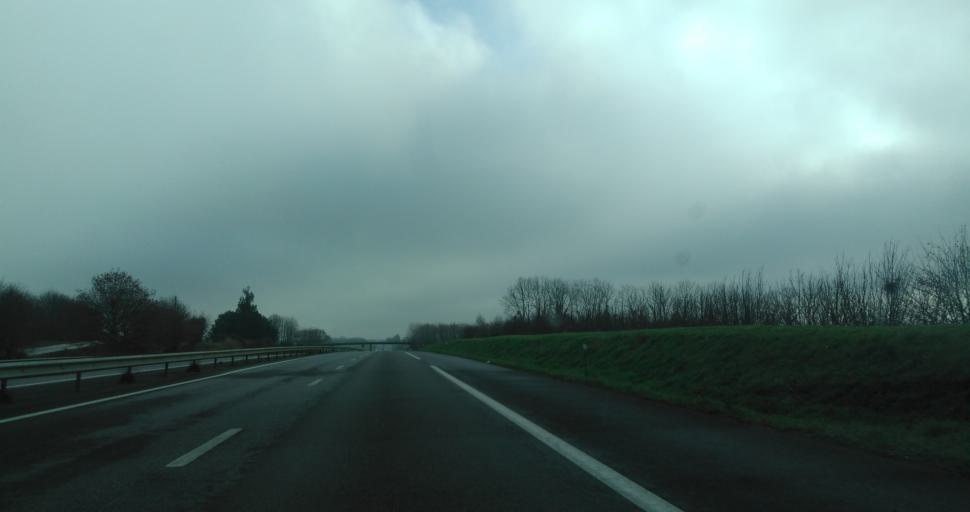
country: FR
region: Brittany
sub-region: Departement d'Ille-et-Vilaine
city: Breteil
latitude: 48.1680
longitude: -1.8756
